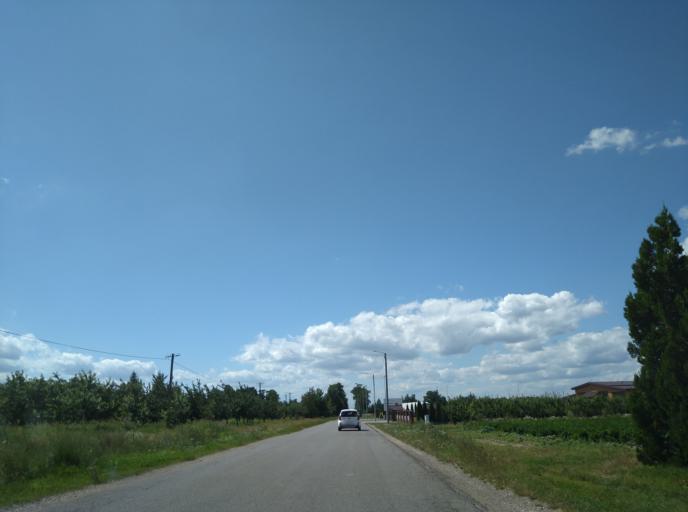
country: PL
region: Masovian Voivodeship
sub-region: Powiat bialobrzeski
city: Bialobrzegi
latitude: 51.6709
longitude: 20.8966
